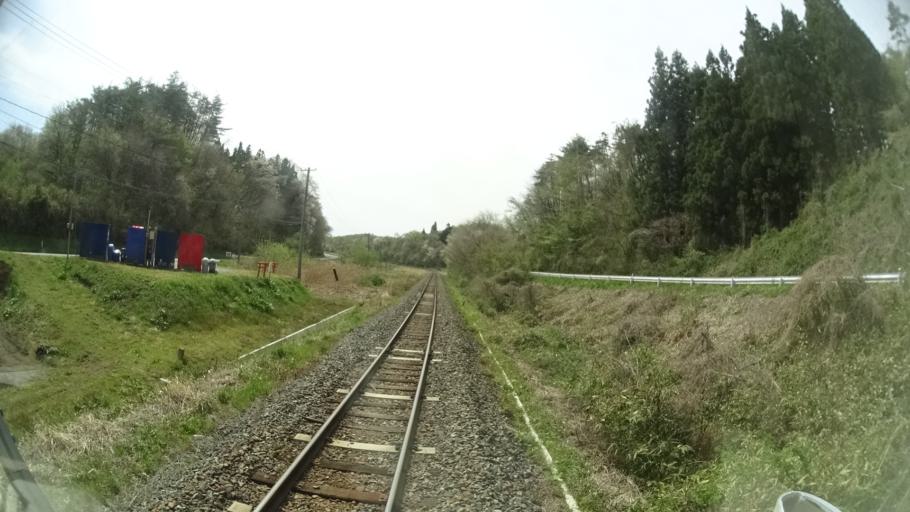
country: JP
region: Iwate
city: Ichinoseki
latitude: 38.9744
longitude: 141.3290
